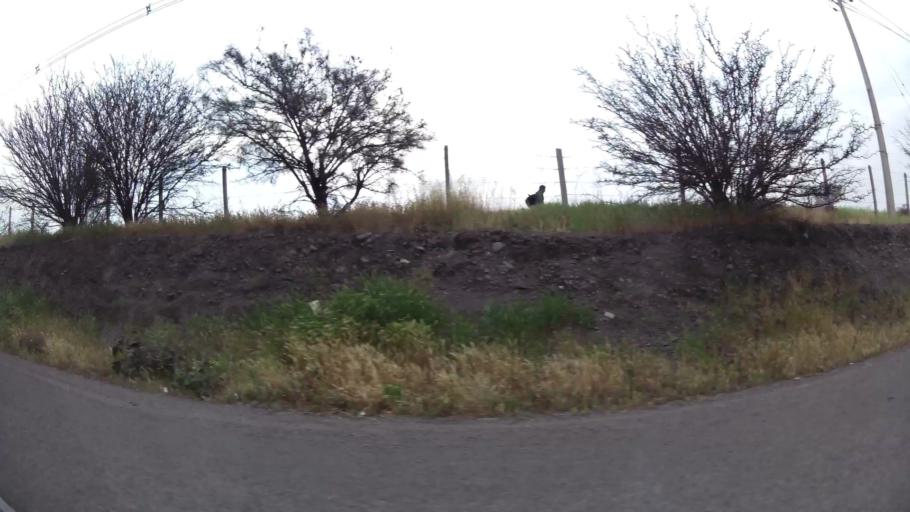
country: CL
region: Santiago Metropolitan
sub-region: Provincia de Chacabuco
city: Chicureo Abajo
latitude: -33.2129
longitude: -70.6723
